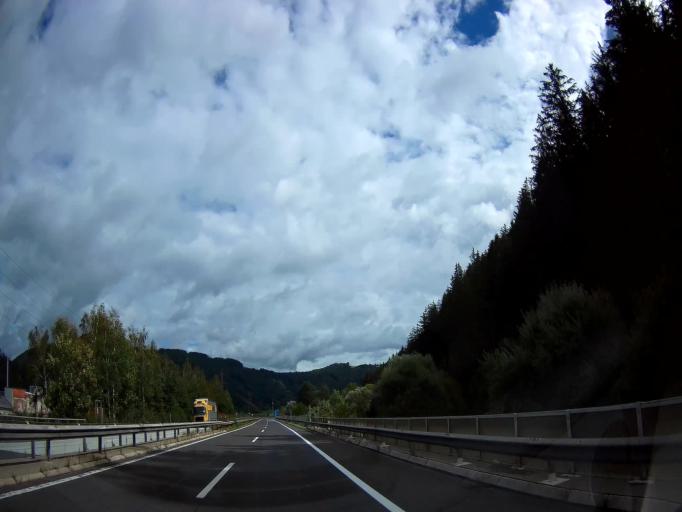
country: AT
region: Styria
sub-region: Politischer Bezirk Leoben
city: Traboch
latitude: 47.3733
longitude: 14.9724
